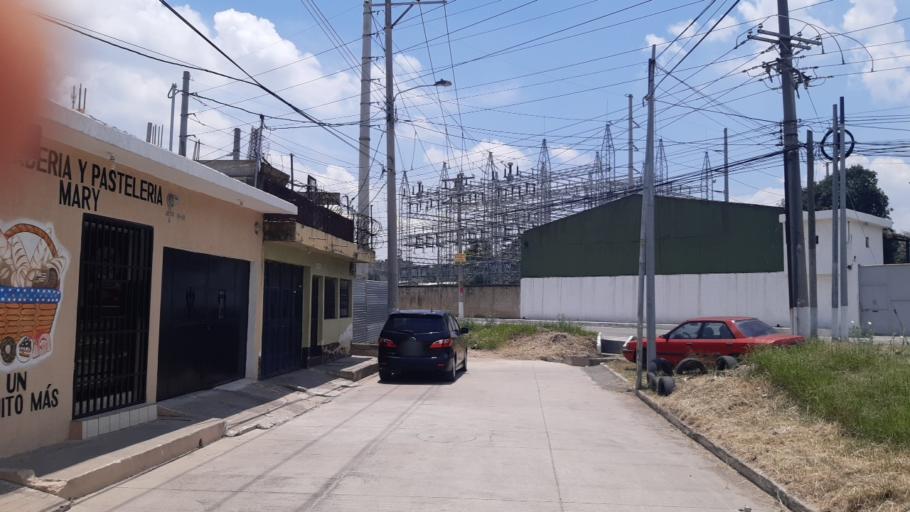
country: GT
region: Guatemala
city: Petapa
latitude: 14.5116
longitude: -90.5584
